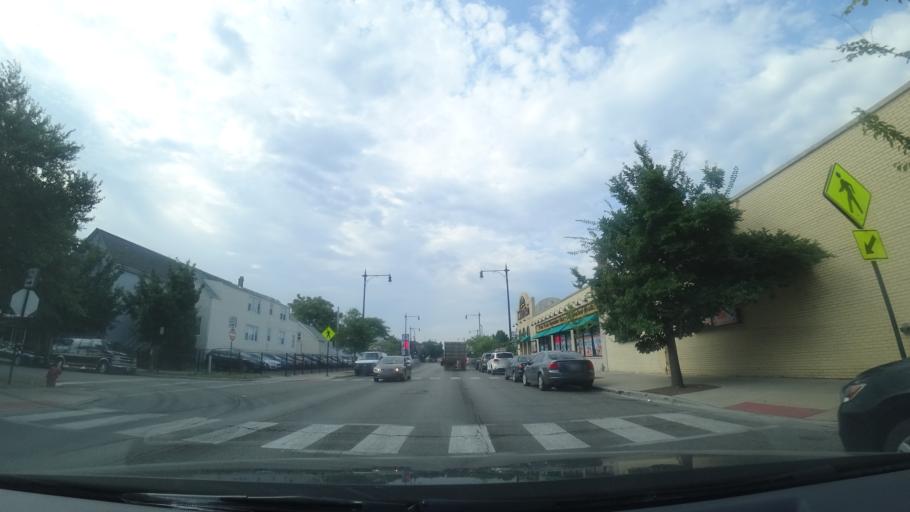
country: US
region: Illinois
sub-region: Cook County
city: Elmwood Park
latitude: 41.9288
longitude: -87.7662
